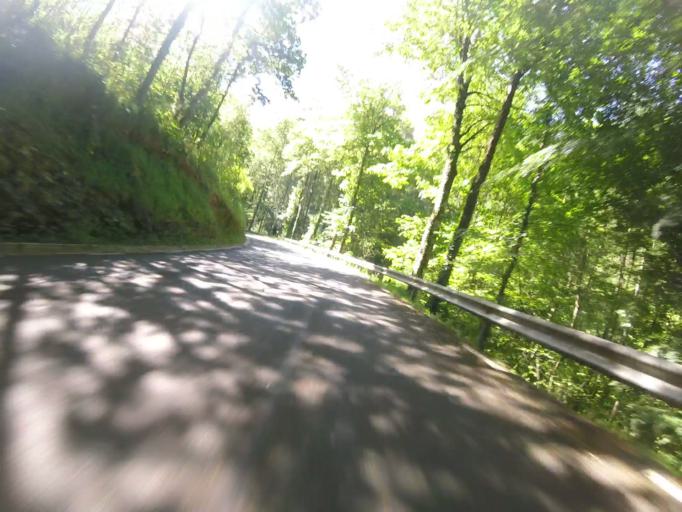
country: ES
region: Basque Country
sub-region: Provincia de Guipuzcoa
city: Albiztur
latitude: 43.1231
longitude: -2.1662
